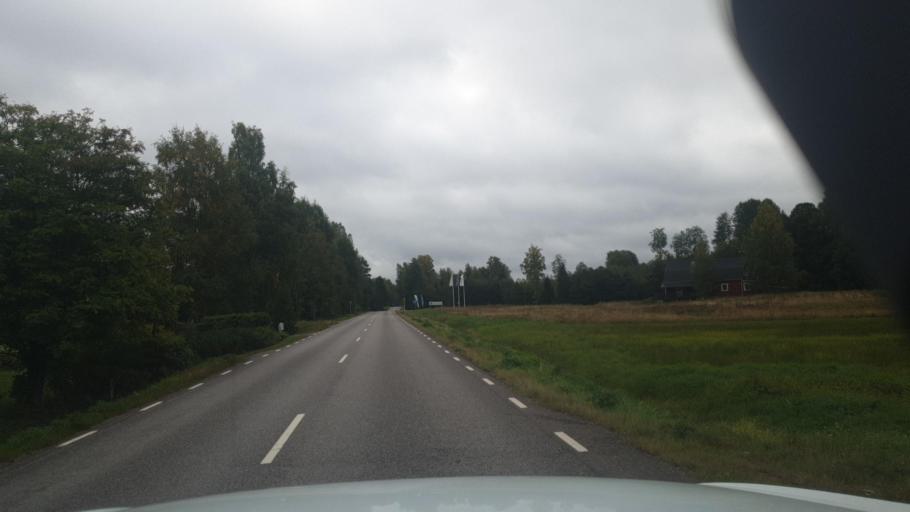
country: SE
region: Vaermland
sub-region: Sunne Kommun
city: Sunne
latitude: 59.8060
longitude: 13.0379
